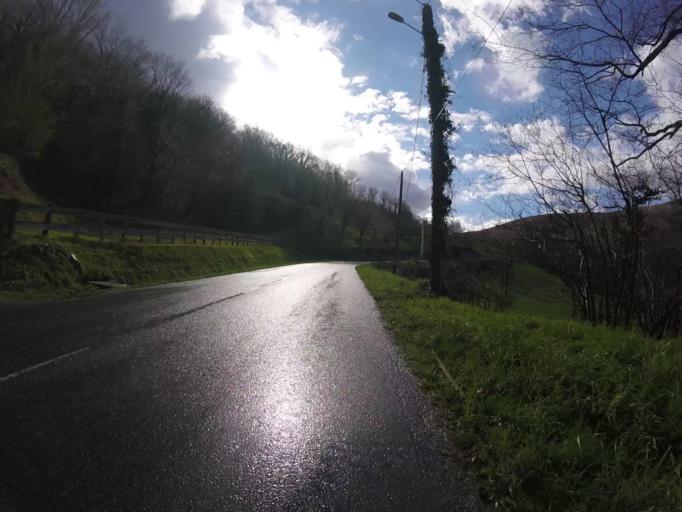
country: FR
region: Aquitaine
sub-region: Departement des Pyrenees-Atlantiques
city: Ascain
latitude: 43.3405
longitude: -1.6160
